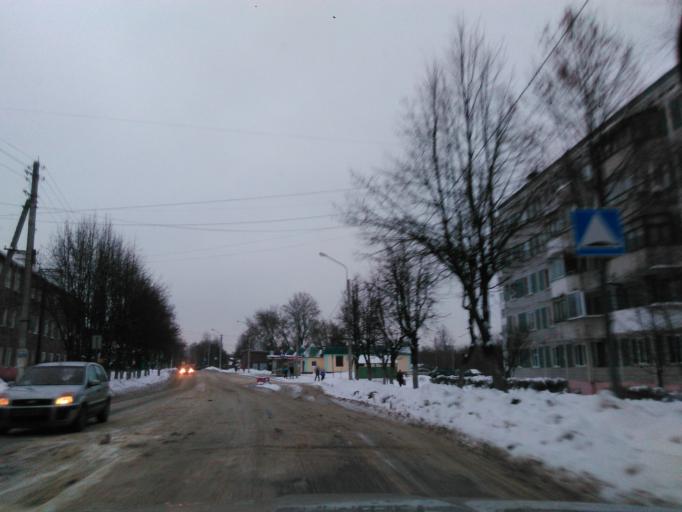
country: RU
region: Moskovskaya
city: Yakhroma
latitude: 56.2870
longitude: 37.4870
